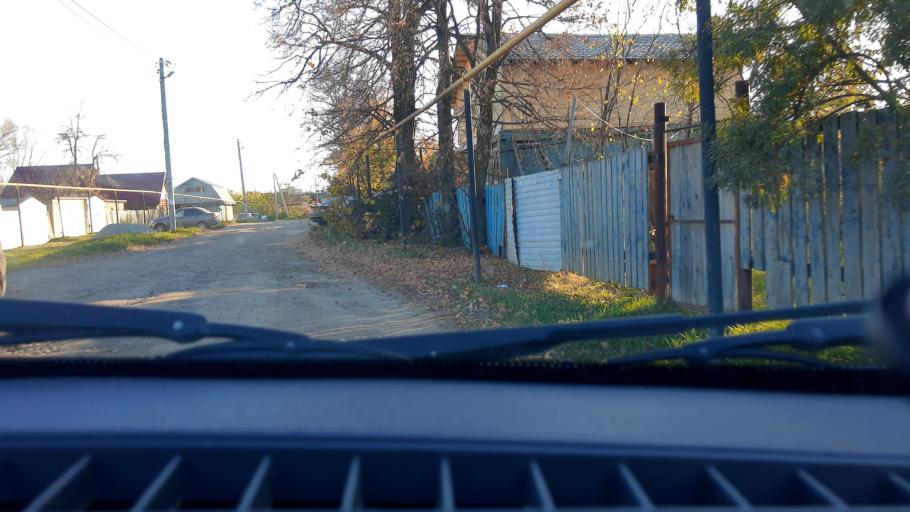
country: RU
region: Bashkortostan
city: Ufa
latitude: 54.8291
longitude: 56.1322
